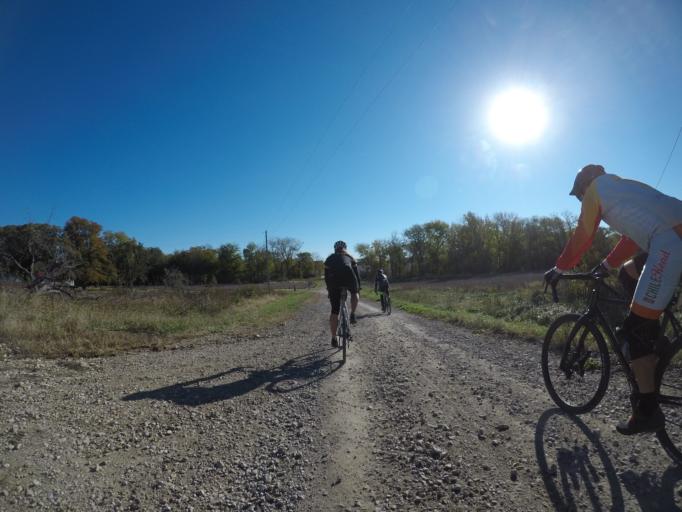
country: US
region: Kansas
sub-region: Morris County
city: Council Grove
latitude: 38.8260
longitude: -96.4642
